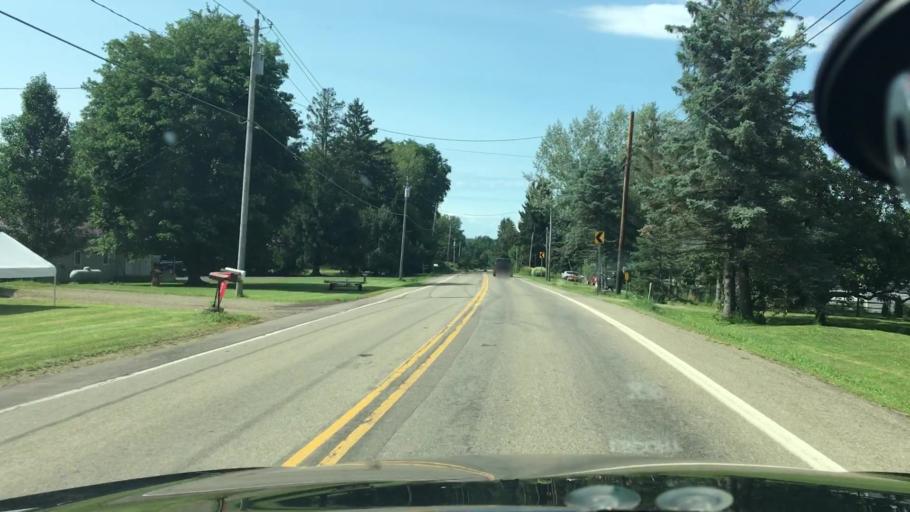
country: US
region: New York
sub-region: Chautauqua County
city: Brocton
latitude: 42.2666
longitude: -79.3506
